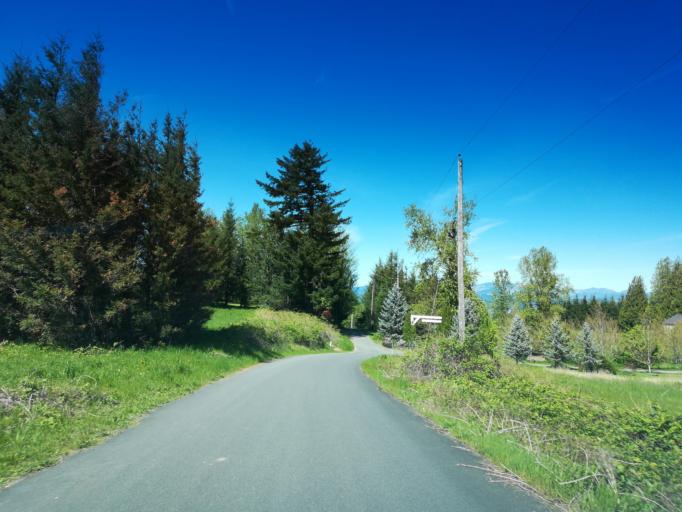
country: US
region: Oregon
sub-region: Multnomah County
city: Troutdale
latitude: 45.5346
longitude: -122.3522
